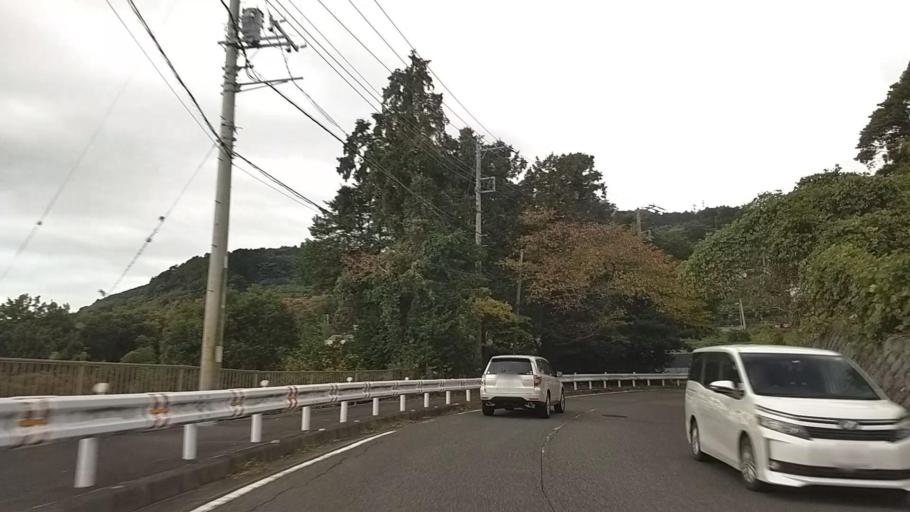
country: JP
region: Kanagawa
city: Odawara
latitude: 35.1928
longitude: 139.1337
